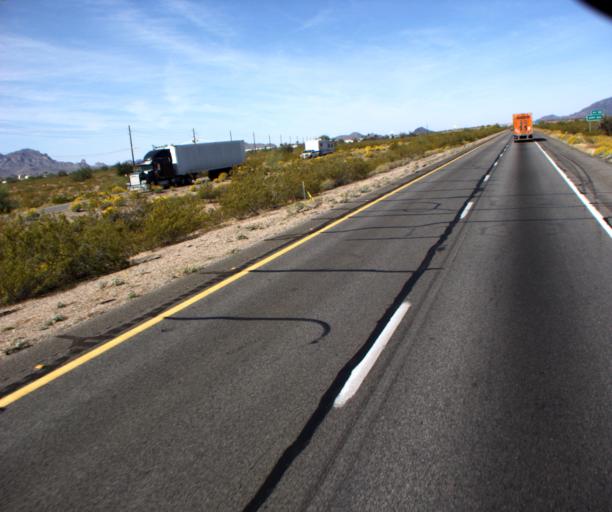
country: US
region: Arizona
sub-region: Maricopa County
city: Buckeye
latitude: 33.4945
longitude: -112.9235
